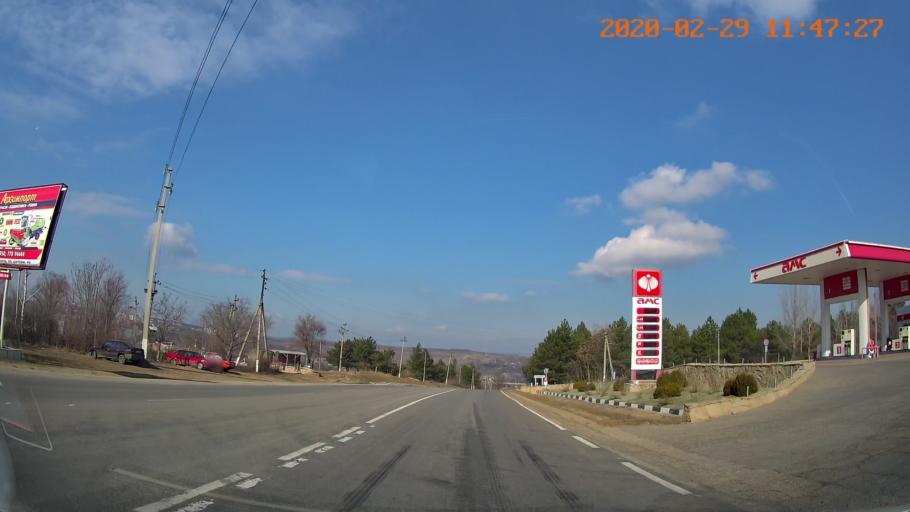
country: MD
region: Rezina
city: Rezina
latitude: 47.7405
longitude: 28.9878
